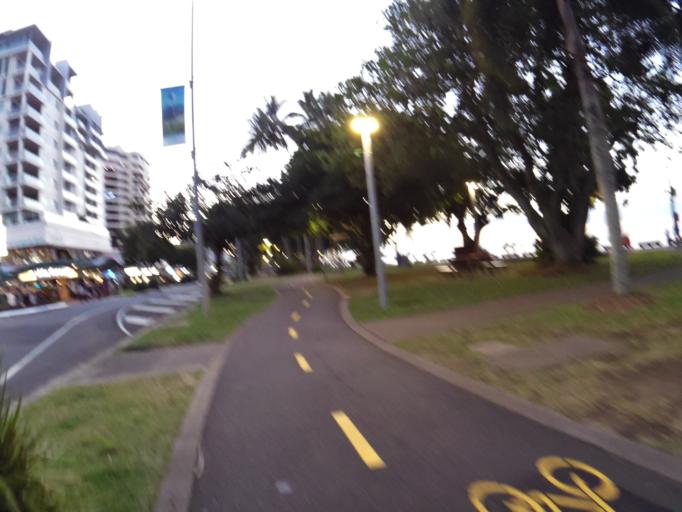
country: AU
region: Queensland
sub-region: Cairns
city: Cairns
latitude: -16.9190
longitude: 145.7765
